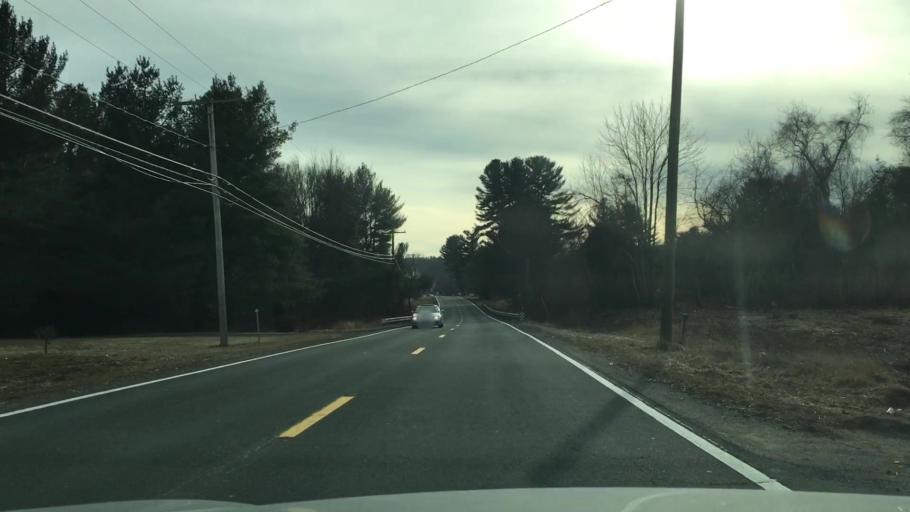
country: US
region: Massachusetts
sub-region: Hampden County
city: Southwick
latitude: 42.0838
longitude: -72.7663
